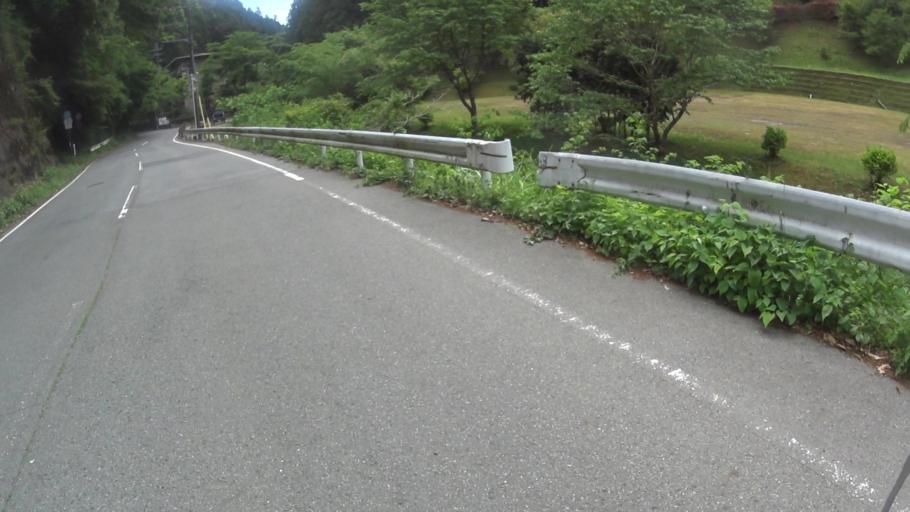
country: JP
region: Nara
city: Yoshino-cho
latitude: 34.3738
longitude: 135.8570
